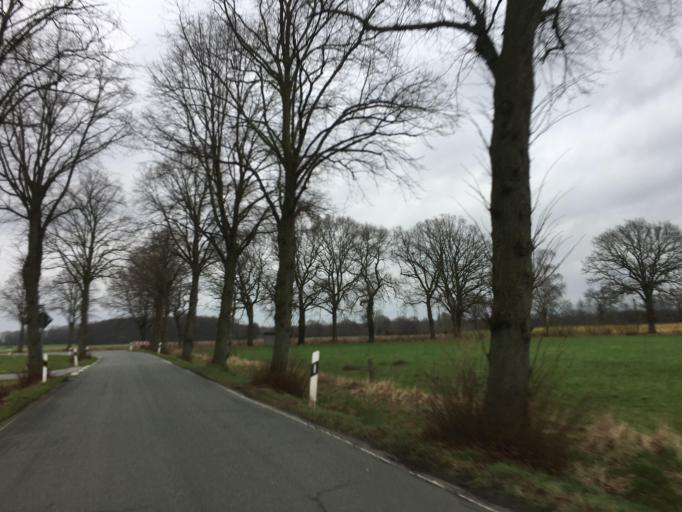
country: DE
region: North Rhine-Westphalia
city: Ludinghausen
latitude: 51.8086
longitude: 7.3995
